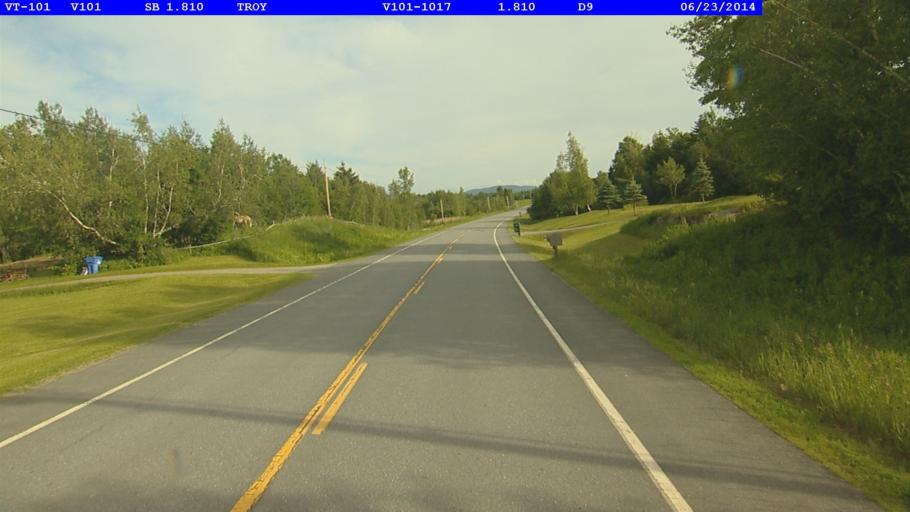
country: US
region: Vermont
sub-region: Orleans County
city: Newport
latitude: 44.9291
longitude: -72.4086
